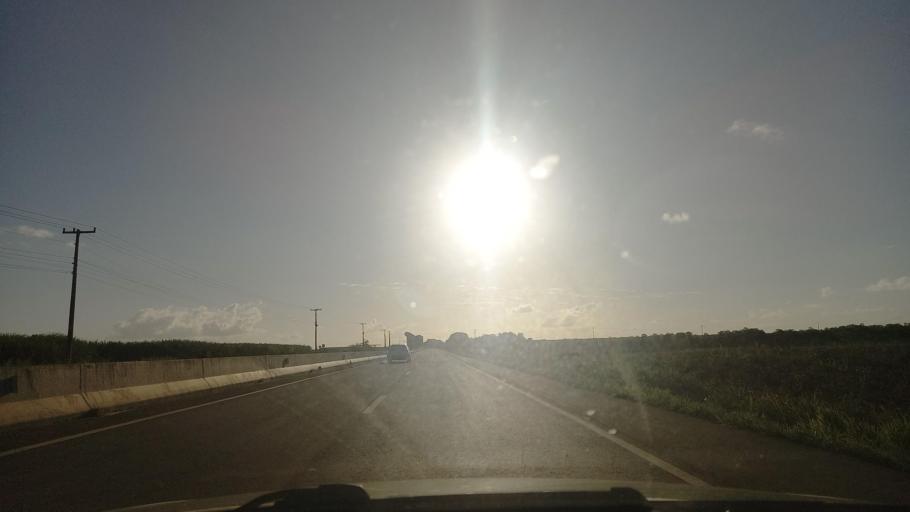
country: BR
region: Alagoas
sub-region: Campo Alegre
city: Campo Alegre
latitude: -9.7935
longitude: -36.3128
